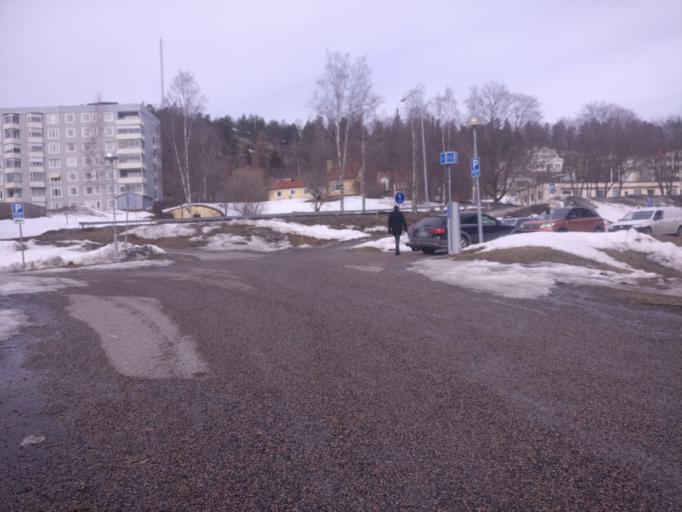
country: SE
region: Vaesternorrland
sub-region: Sundsvalls Kommun
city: Sundsvall
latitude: 62.3947
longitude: 17.3062
